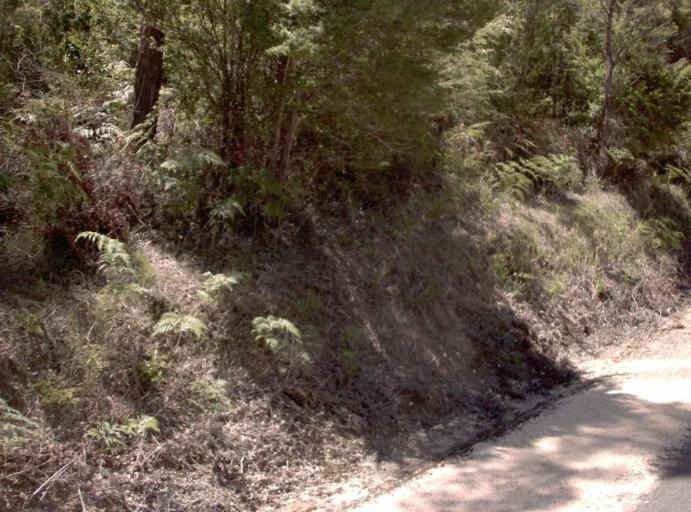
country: AU
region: New South Wales
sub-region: Bombala
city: Bombala
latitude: -37.6280
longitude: 148.8876
